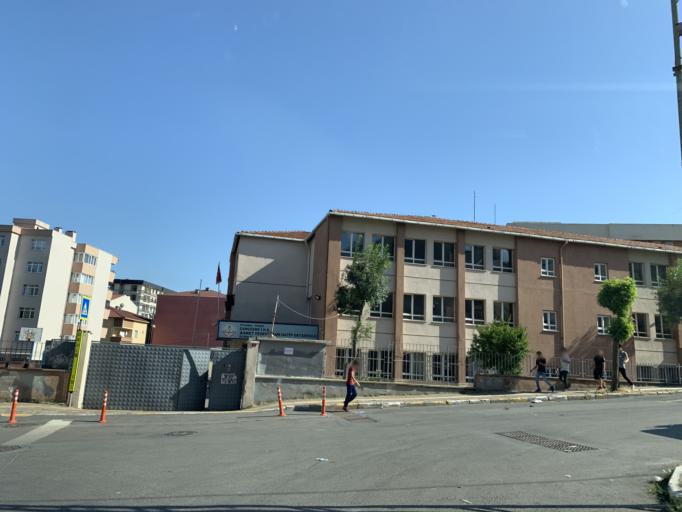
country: TR
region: Istanbul
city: Pendik
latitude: 40.8734
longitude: 29.2754
